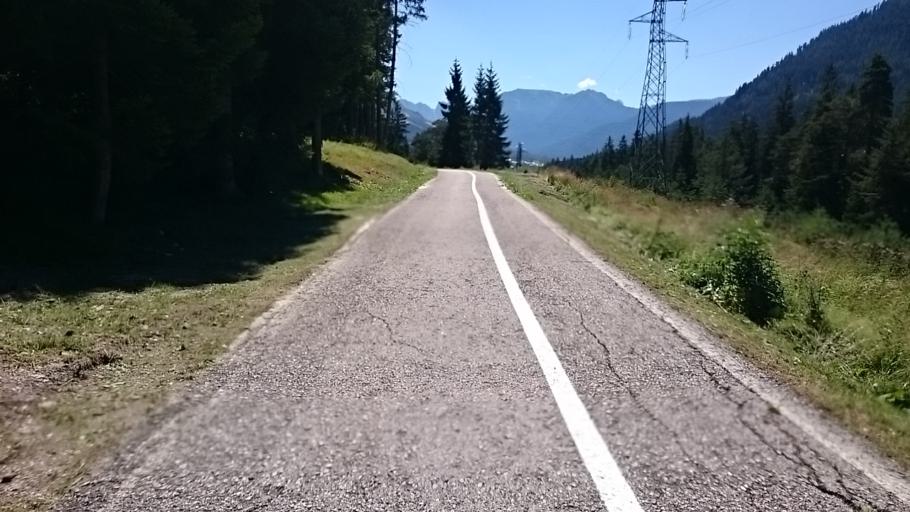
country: IT
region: Veneto
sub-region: Provincia di Belluno
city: San Vito
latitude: 46.4885
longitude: 12.1856
